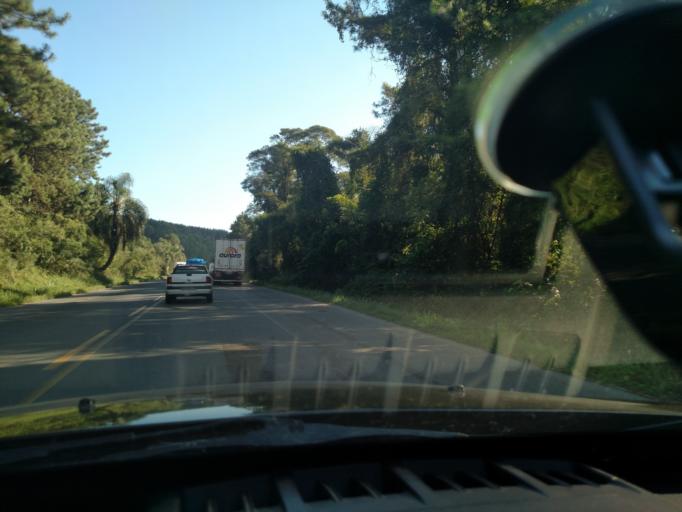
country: BR
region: Santa Catarina
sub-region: Otacilio Costa
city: Otacilio Costa
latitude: -27.2724
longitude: -50.0626
